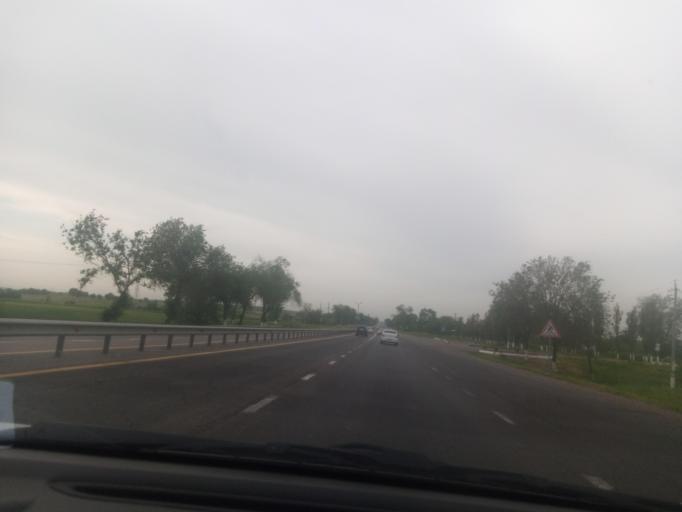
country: UZ
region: Toshkent
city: Tuytepa
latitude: 41.0779
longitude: 69.4718
